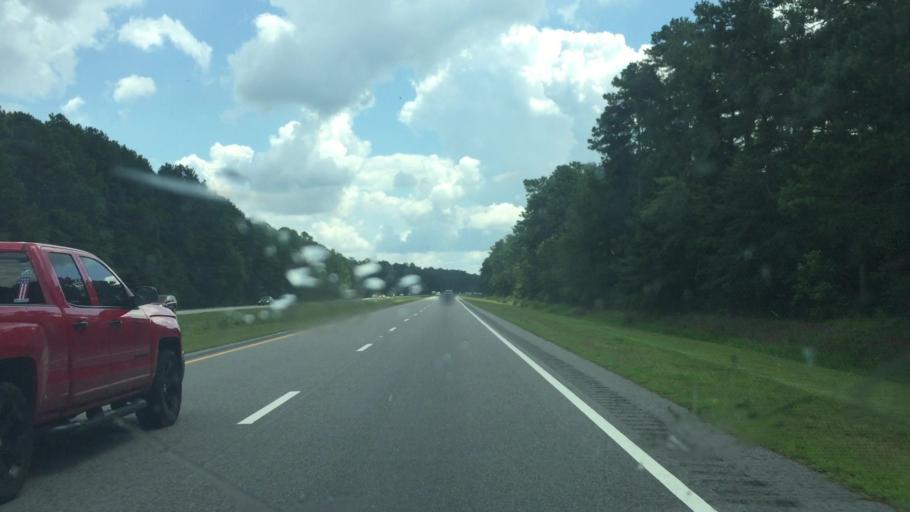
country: US
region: North Carolina
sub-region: Columbus County
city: Chadbourn
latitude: 34.3835
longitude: -78.8629
